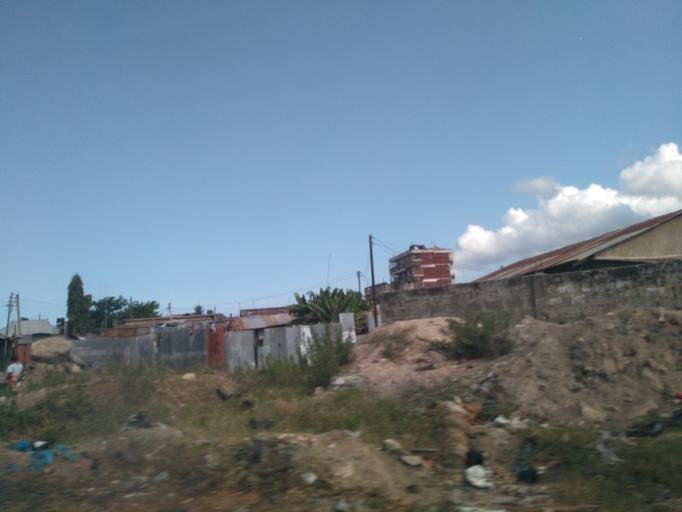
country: TZ
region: Dar es Salaam
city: Magomeni
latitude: -6.7660
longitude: 39.2651
